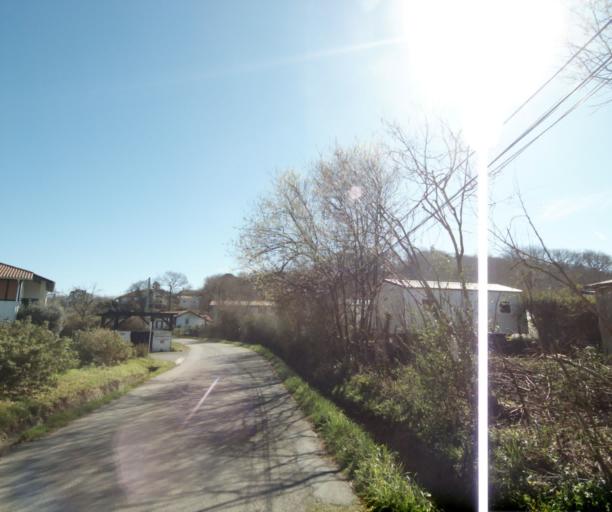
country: FR
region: Aquitaine
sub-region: Departement des Pyrenees-Atlantiques
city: Ciboure
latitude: 43.3827
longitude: -1.6951
